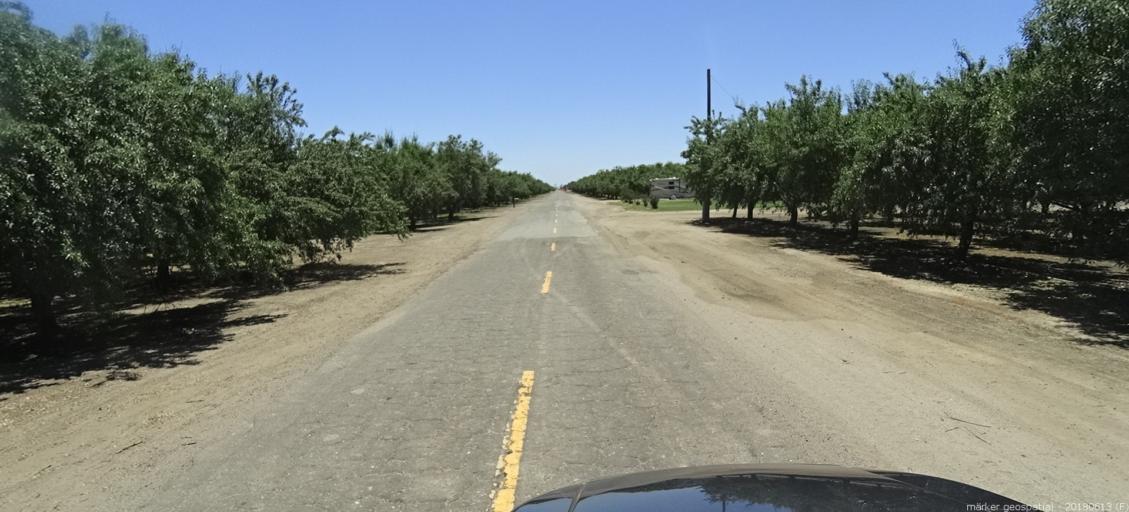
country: US
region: California
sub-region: Madera County
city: Chowchilla
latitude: 37.0513
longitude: -120.2745
